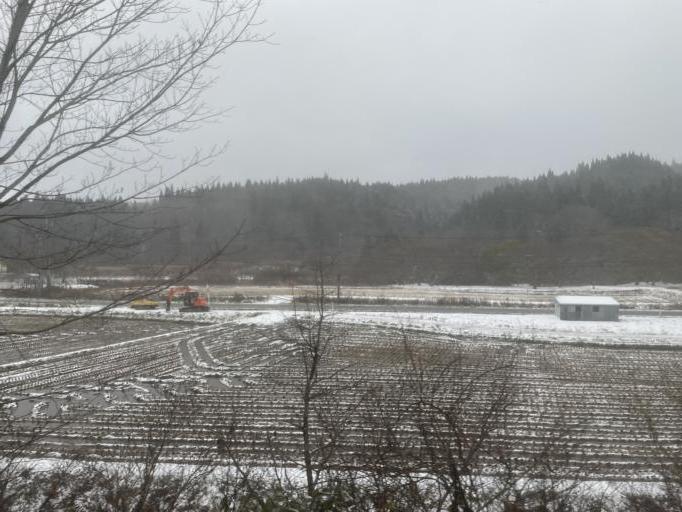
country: JP
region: Aomori
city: Goshogawara
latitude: 41.1326
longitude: 140.5185
